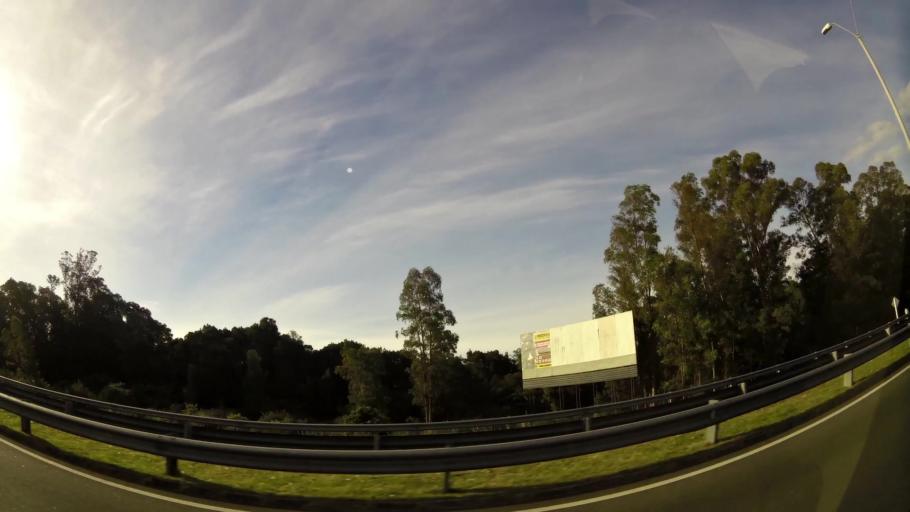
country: UY
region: Maldonado
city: Piriapolis
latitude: -34.7787
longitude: -55.3568
